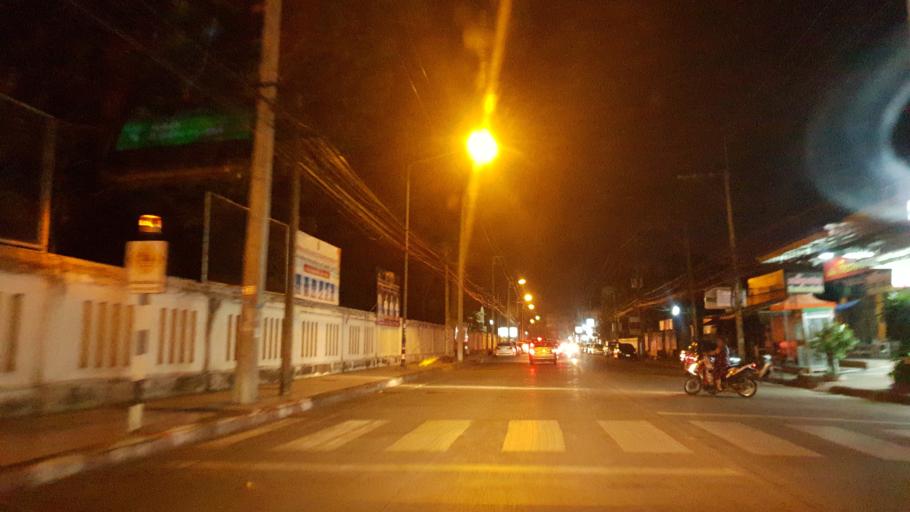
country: TH
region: Phitsanulok
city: Phitsanulok
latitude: 16.8096
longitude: 100.2700
